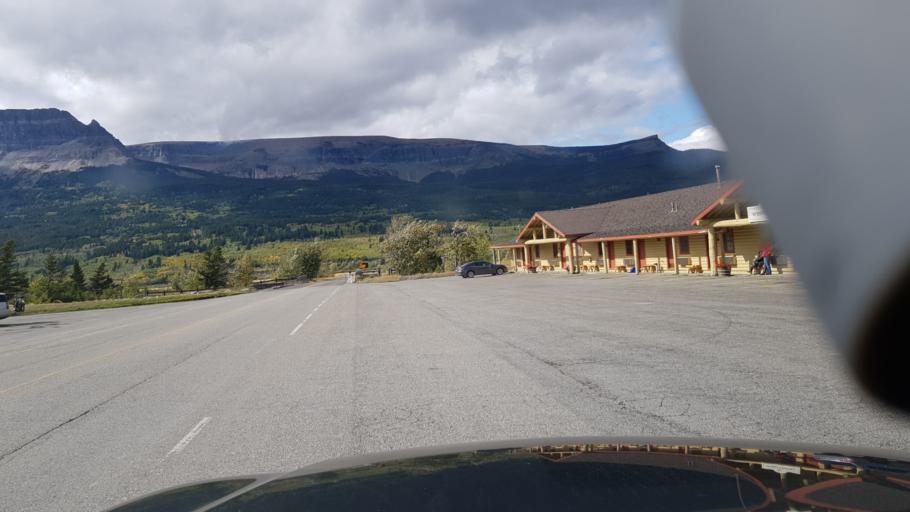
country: US
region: Montana
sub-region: Glacier County
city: North Browning
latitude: 48.7439
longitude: -113.4300
